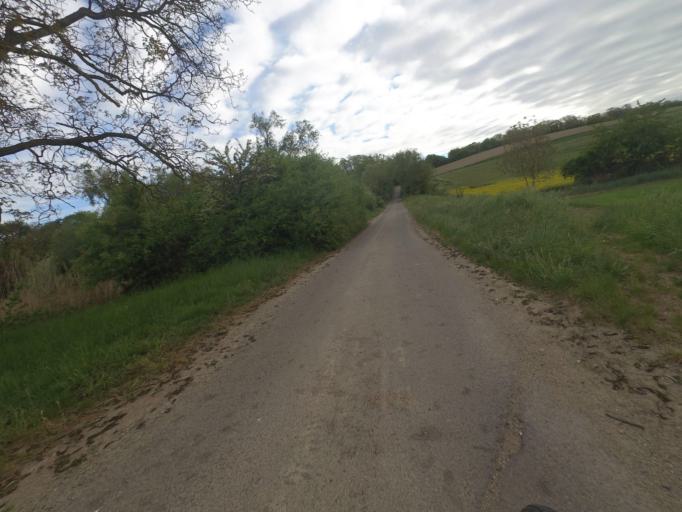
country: DE
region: Rheinland-Pfalz
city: Kirchheimbolanden
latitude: 49.6793
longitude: 8.0153
